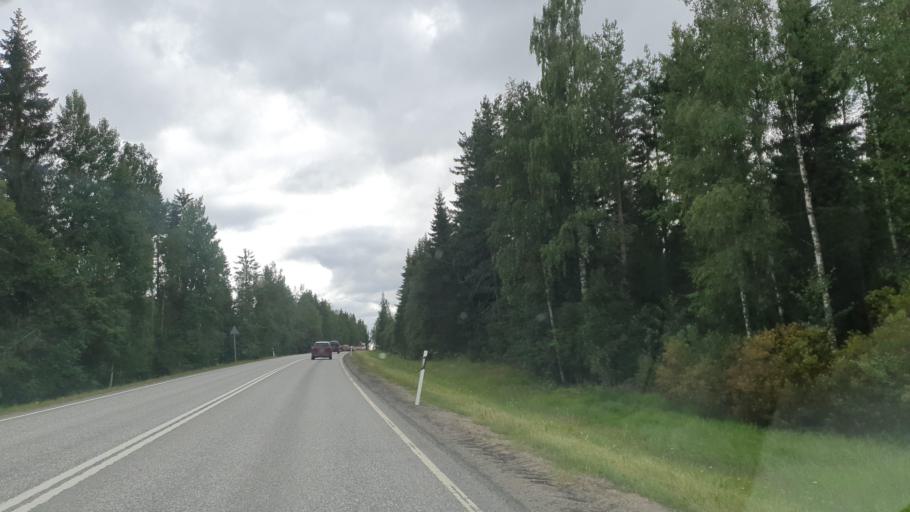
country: FI
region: Northern Savo
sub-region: Ylae-Savo
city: Sonkajaervi
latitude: 63.6850
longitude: 27.3394
